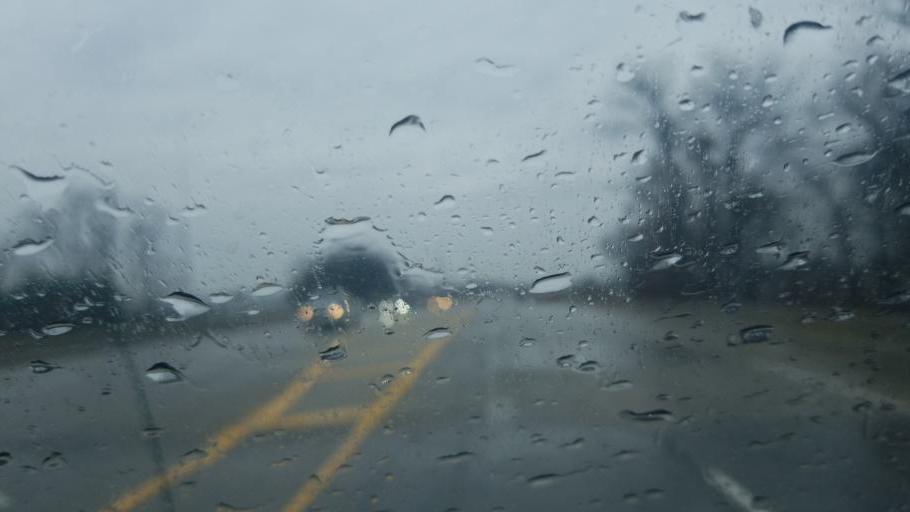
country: US
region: Indiana
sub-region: Bartholomew County
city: Columbus
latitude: 39.2081
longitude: -85.8727
